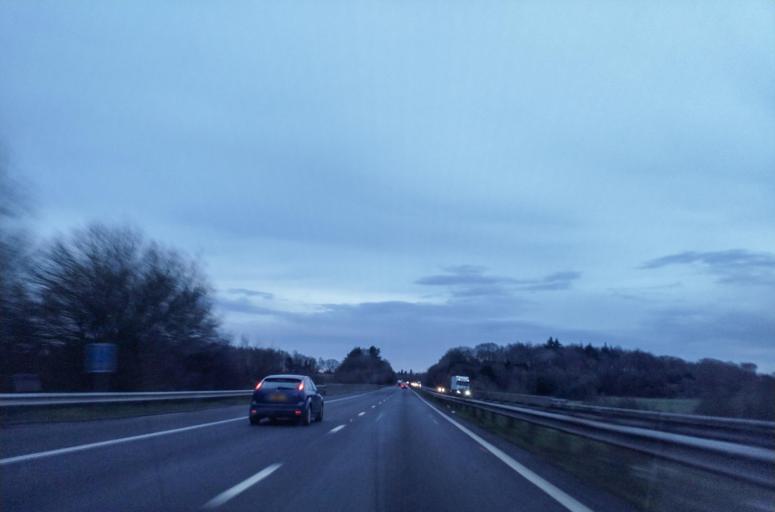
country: GB
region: England
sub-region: Kent
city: Sittingbourne
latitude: 51.3037
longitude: 0.7245
